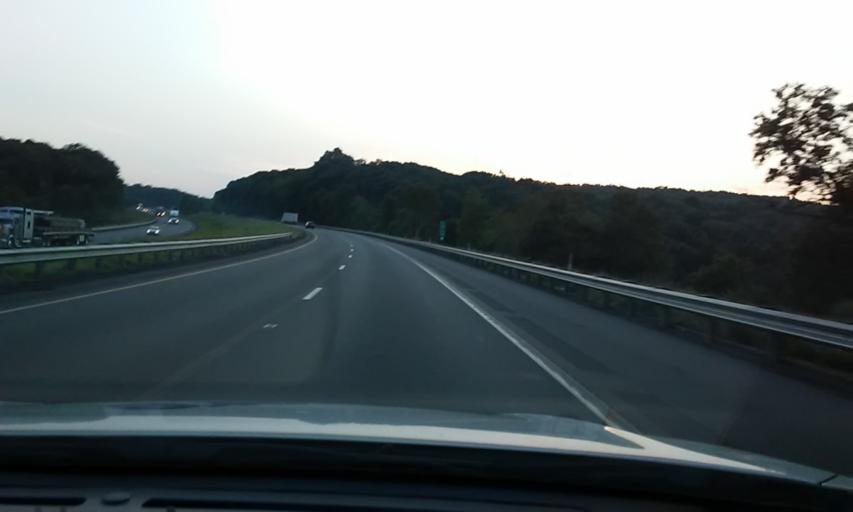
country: US
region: Pennsylvania
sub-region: Clarion County
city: Marianne
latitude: 41.1977
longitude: -79.4685
